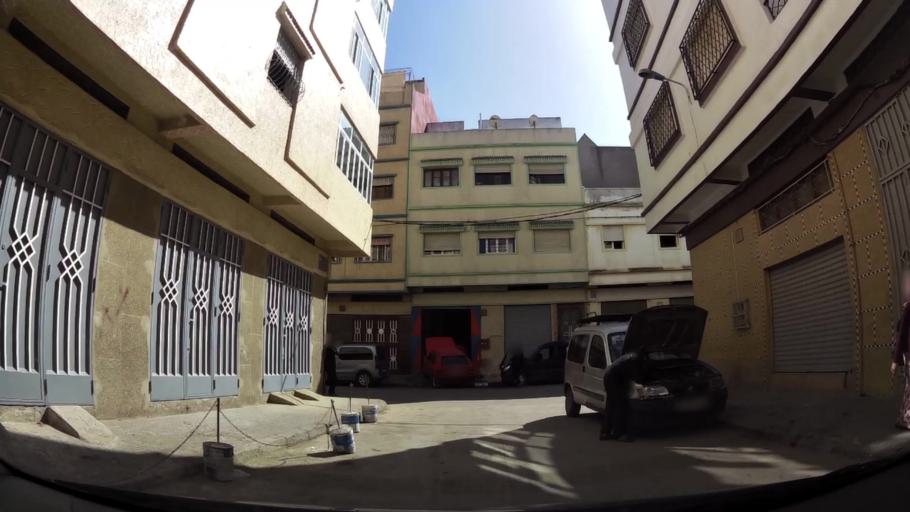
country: MA
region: Tanger-Tetouan
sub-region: Tanger-Assilah
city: Tangier
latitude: 35.7522
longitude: -5.8074
